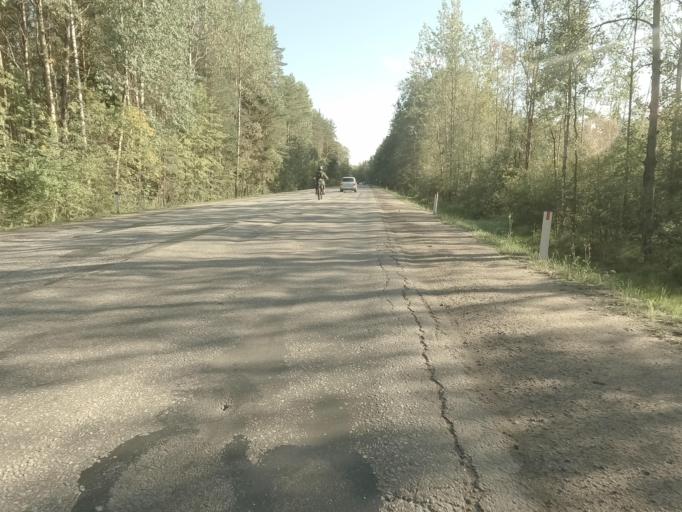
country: RU
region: Leningrad
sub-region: Volosovskiy Rayon
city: Shlissel'burg
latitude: 59.9437
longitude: 30.9841
